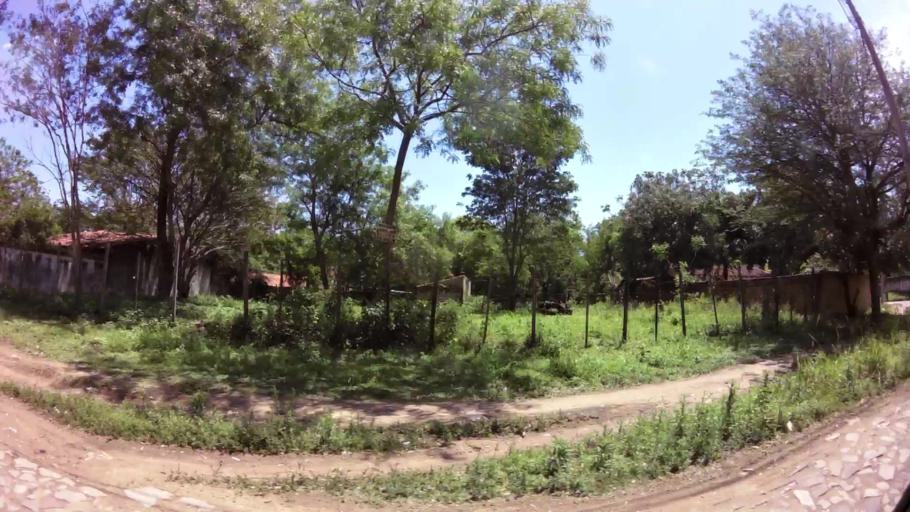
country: PY
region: Central
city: Colonia Mariano Roque Alonso
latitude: -25.1968
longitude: -57.5477
